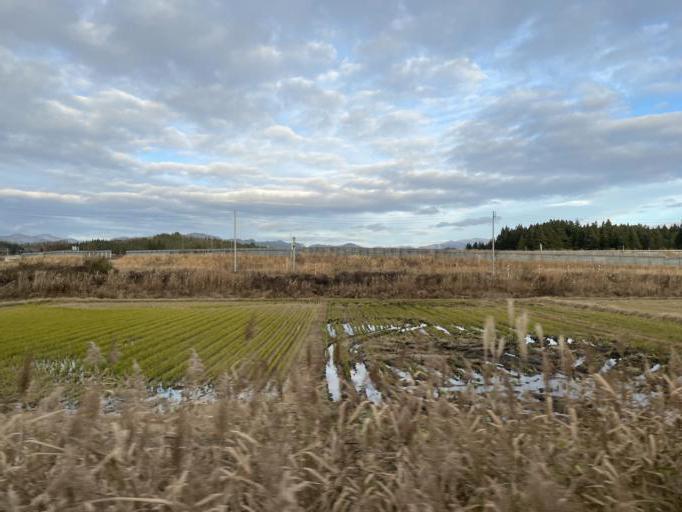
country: JP
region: Yamagata
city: Obanazawa
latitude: 38.6352
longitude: 140.3697
